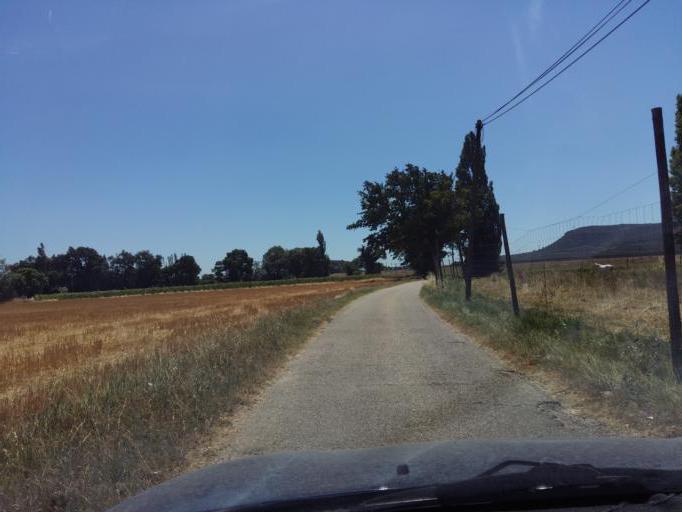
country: FR
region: Provence-Alpes-Cote d'Azur
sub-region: Departement du Vaucluse
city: Mornas
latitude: 44.1735
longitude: 4.7318
